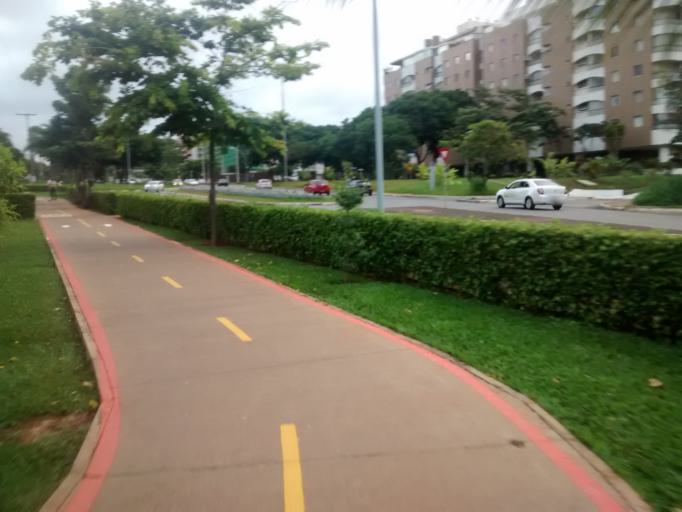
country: BR
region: Federal District
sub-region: Brasilia
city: Brasilia
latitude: -15.7576
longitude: -47.8891
